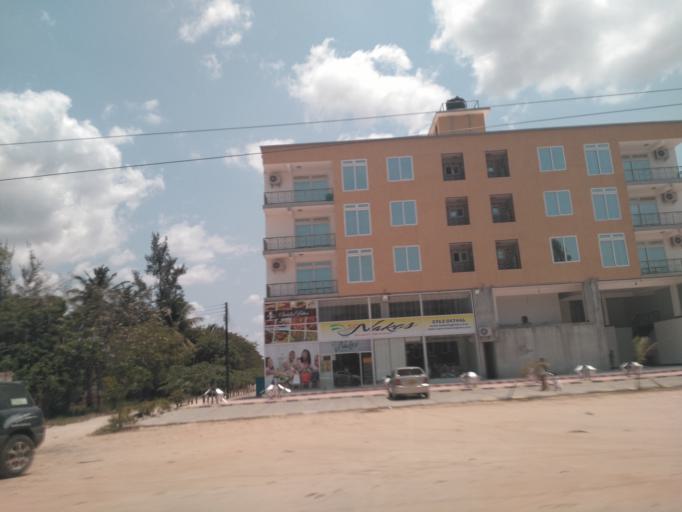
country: TZ
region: Dar es Salaam
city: Dar es Salaam
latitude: -6.8284
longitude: 39.3323
